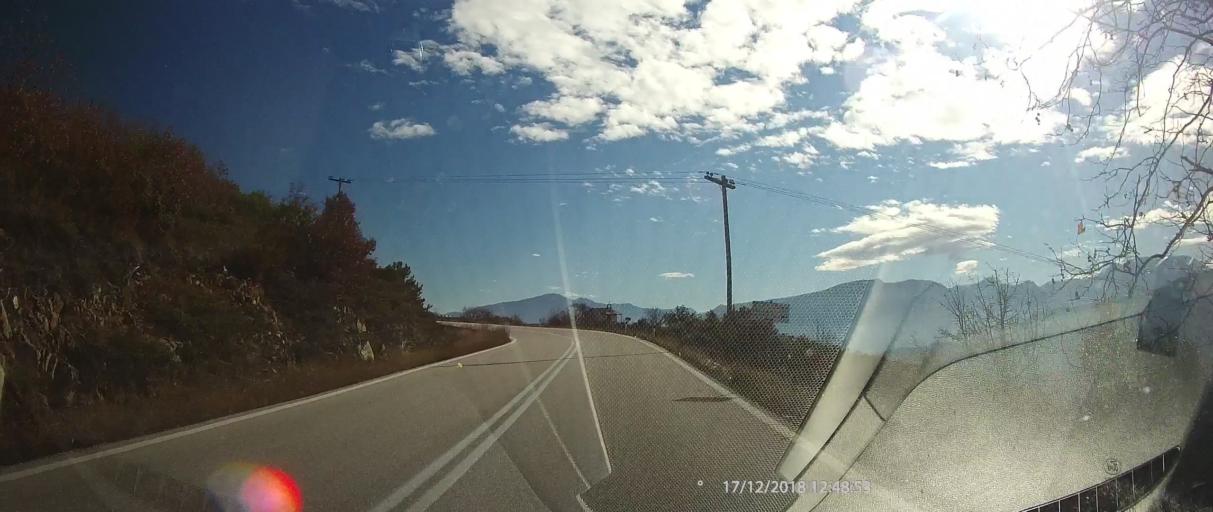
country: GR
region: Thessaly
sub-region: Trikala
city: Kastraki
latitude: 39.7820
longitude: 21.4393
